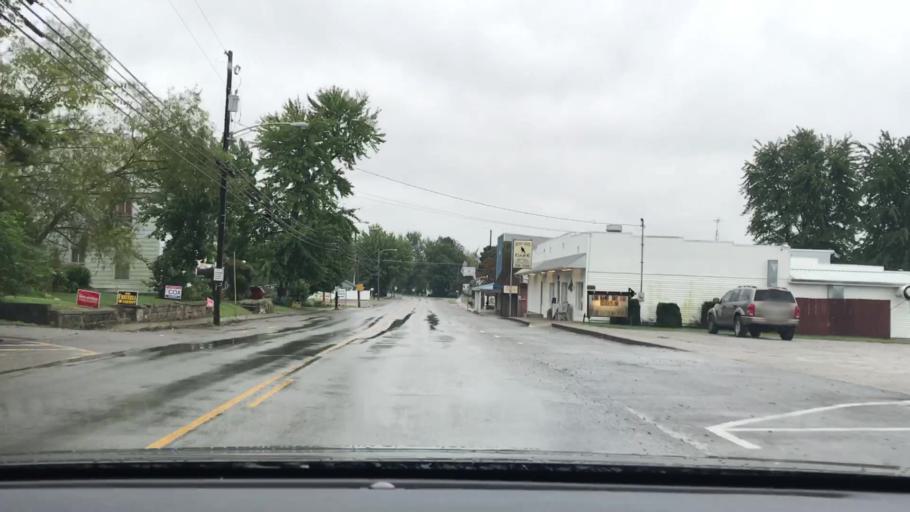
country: US
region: Kentucky
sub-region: McLean County
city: Calhoun
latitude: 37.4171
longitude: -87.2662
